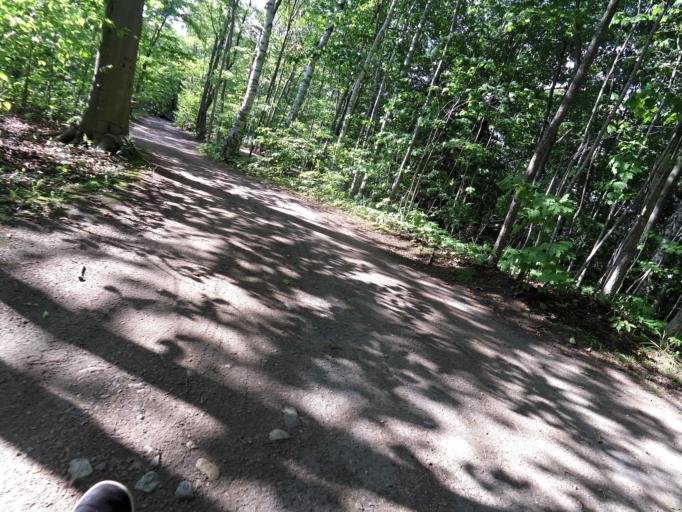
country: CA
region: Ontario
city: Tobermory
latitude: 45.2282
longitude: -81.6456
